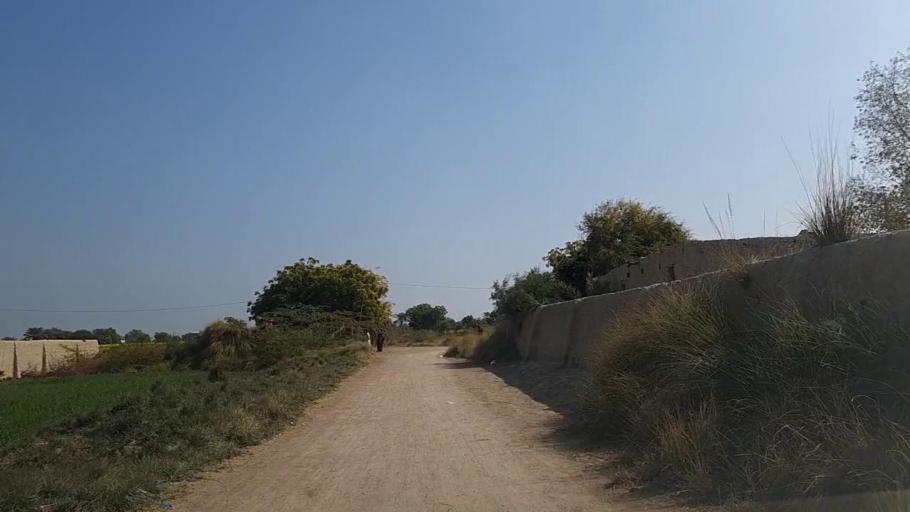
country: PK
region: Sindh
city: Nawabshah
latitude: 26.2504
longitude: 68.4923
